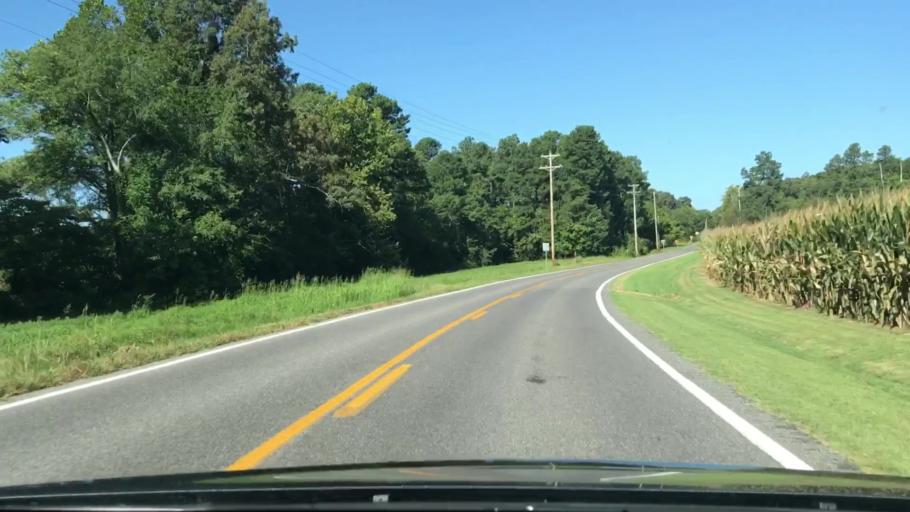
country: US
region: Kentucky
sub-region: Graves County
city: Mayfield
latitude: 36.7744
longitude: -88.4835
